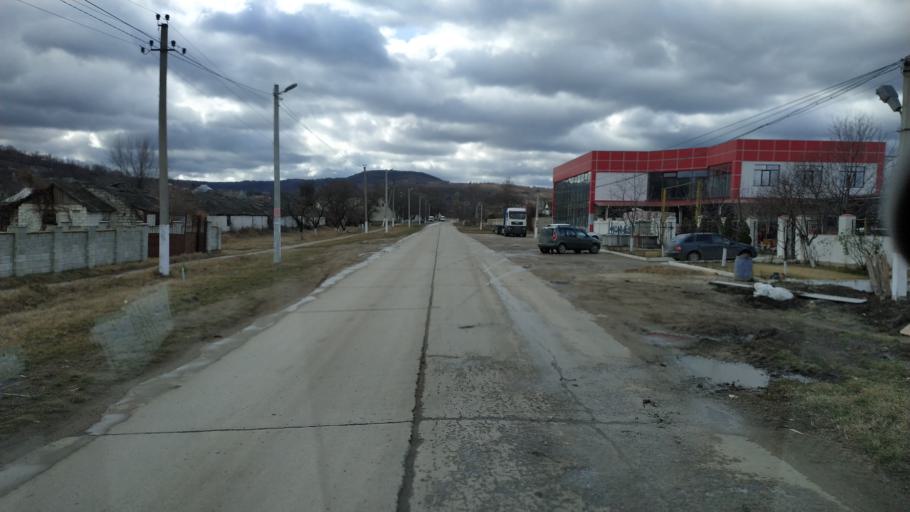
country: MD
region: Stinga Nistrului
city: Bucovat
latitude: 47.1430
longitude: 28.3896
